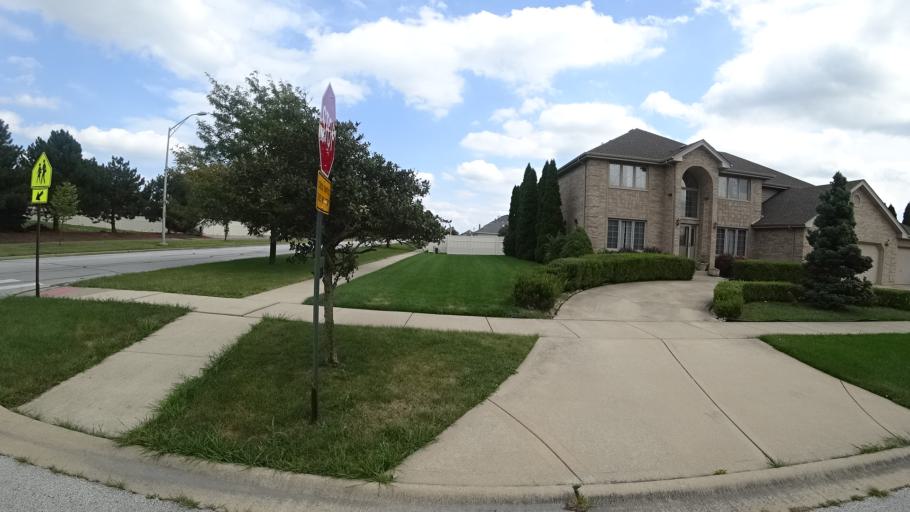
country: US
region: Illinois
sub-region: Cook County
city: Orland Hills
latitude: 41.5653
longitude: -87.8167
